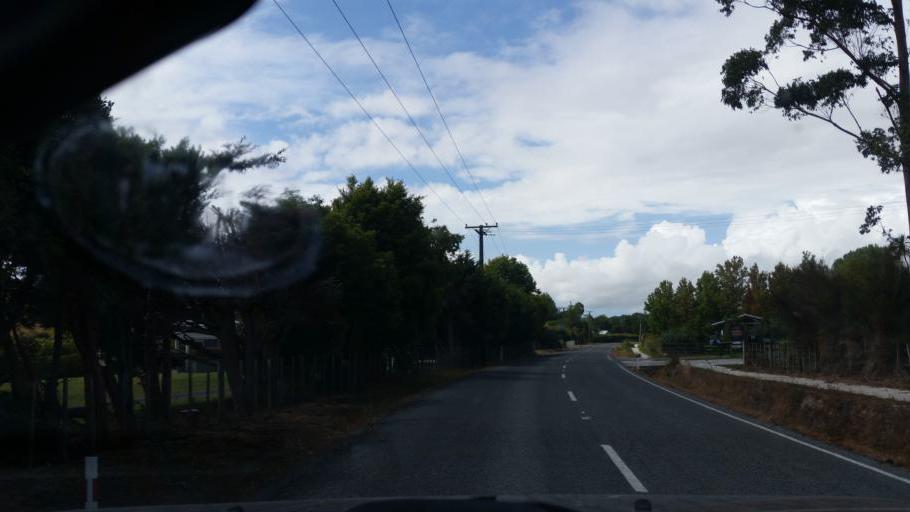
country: NZ
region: Auckland
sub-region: Auckland
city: Wellsford
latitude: -36.1237
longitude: 174.5571
